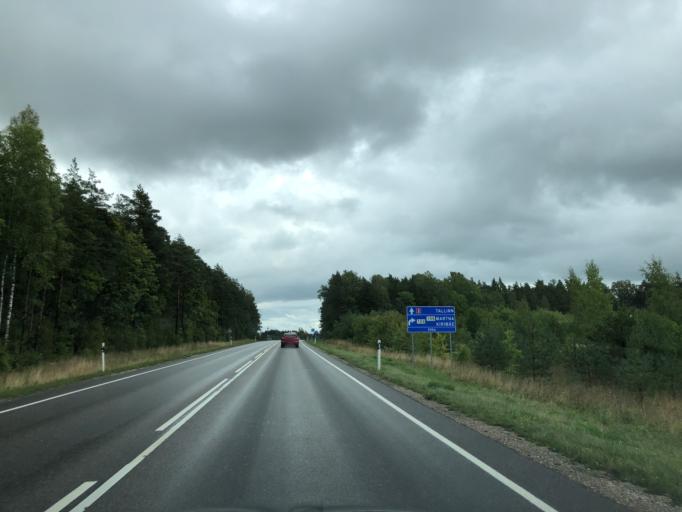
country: EE
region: Laeaene
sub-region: Ridala Parish
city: Uuemoisa
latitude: 58.9581
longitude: 23.7192
